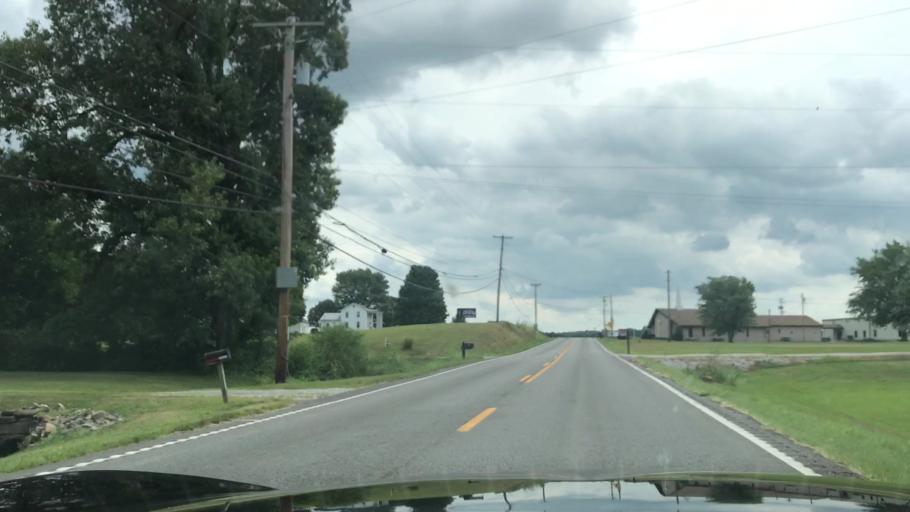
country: US
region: Kentucky
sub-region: Muhlenberg County
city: Greenville
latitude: 37.1997
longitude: -87.1339
